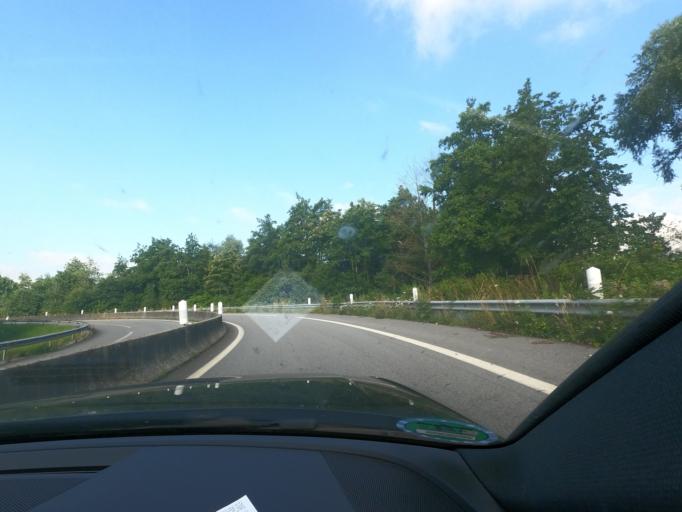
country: FR
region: Haute-Normandie
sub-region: Departement de la Seine-Maritime
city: Yerville
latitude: 49.6533
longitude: 0.8462
